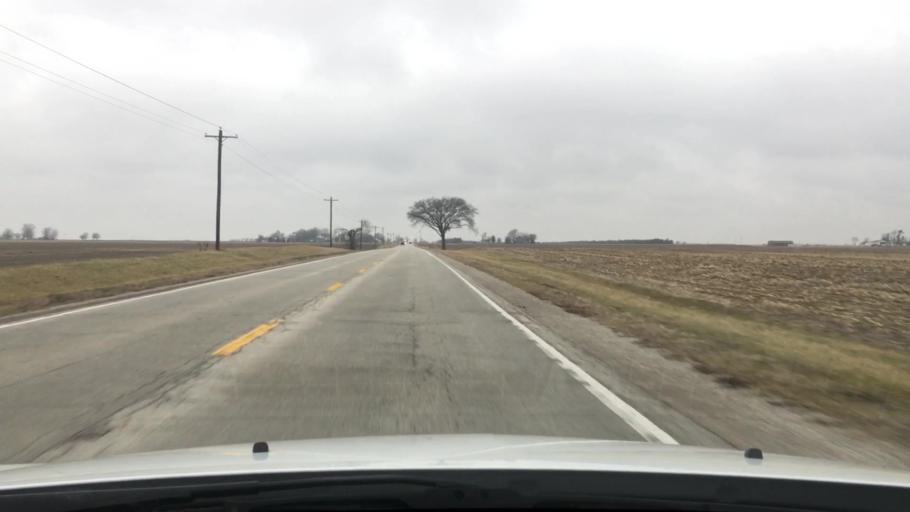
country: US
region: Illinois
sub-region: Iroquois County
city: Clifton
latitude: 40.8875
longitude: -87.8526
